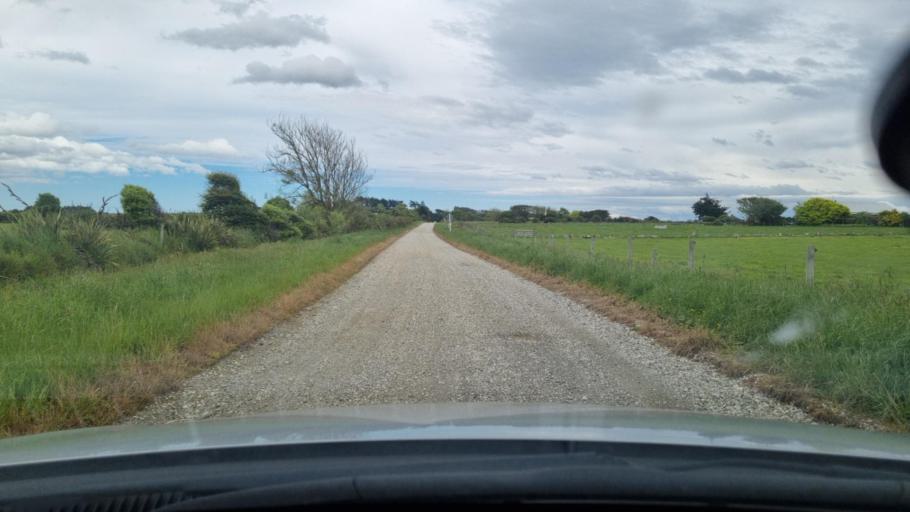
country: NZ
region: Southland
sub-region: Invercargill City
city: Invercargill
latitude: -46.4020
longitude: 168.2597
